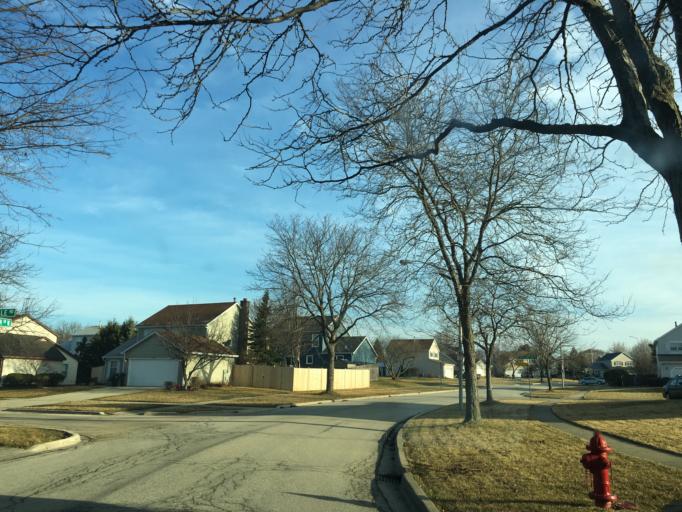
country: US
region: Illinois
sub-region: Cook County
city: Schaumburg
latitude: 42.0460
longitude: -88.1125
